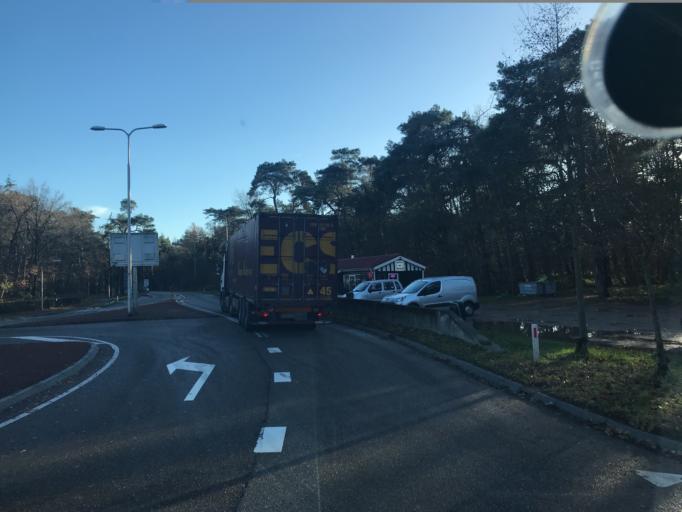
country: NL
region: Gelderland
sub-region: Gemeente Harderwijk
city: Harderwijk
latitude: 52.3314
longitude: 5.6404
